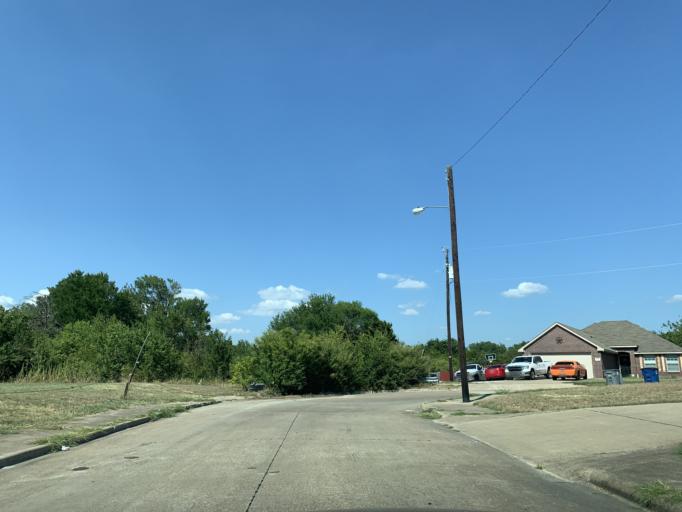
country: US
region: Texas
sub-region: Dallas County
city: Hutchins
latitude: 32.6594
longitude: -96.7775
